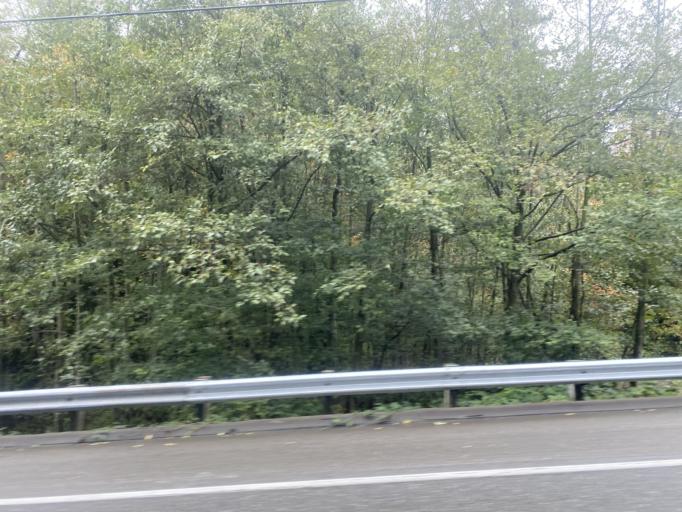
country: US
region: Washington
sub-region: Snohomish County
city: Mukilteo
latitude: 47.9377
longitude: -122.3060
